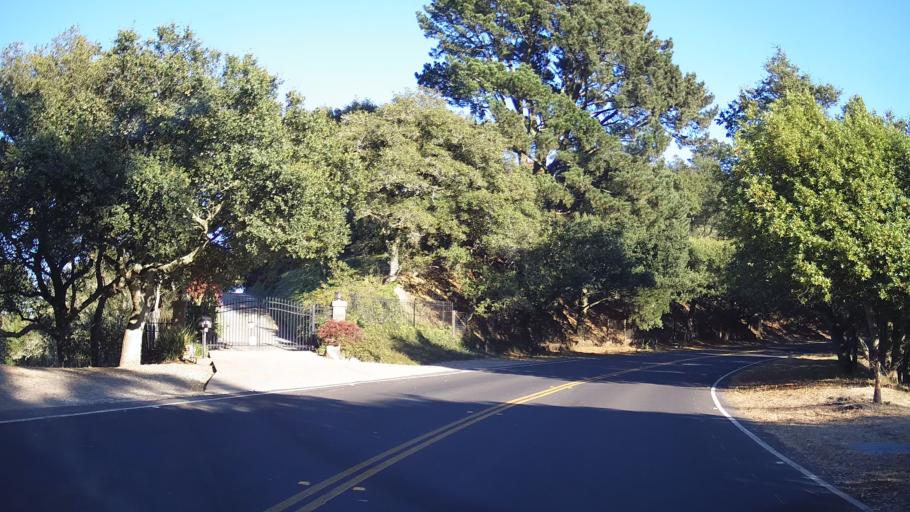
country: US
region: California
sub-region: Alameda County
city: Piedmont
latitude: 37.8569
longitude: -122.2120
